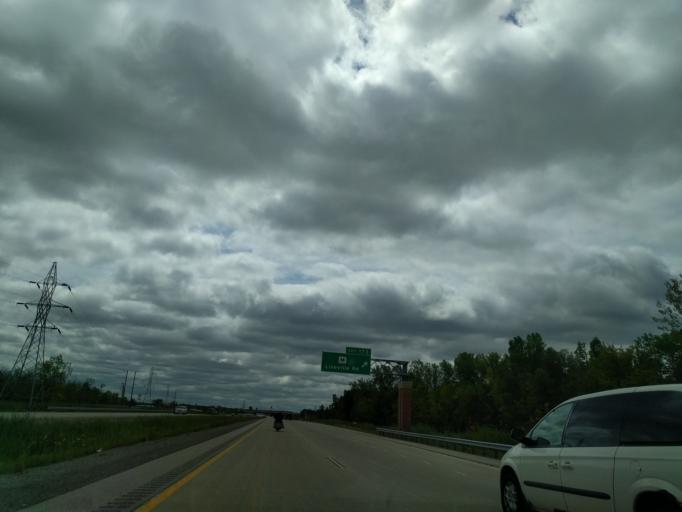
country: US
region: Wisconsin
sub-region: Brown County
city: Suamico
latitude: 44.5986
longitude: -88.0498
